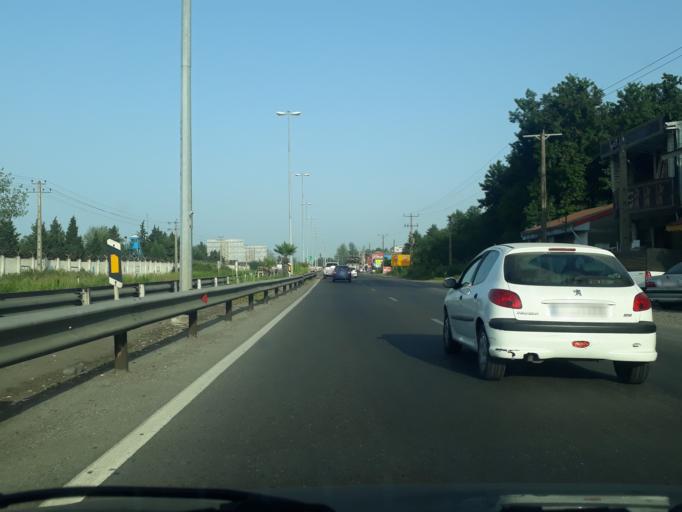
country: IR
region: Gilan
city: Bandar-e Anzali
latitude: 37.4579
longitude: 49.6066
